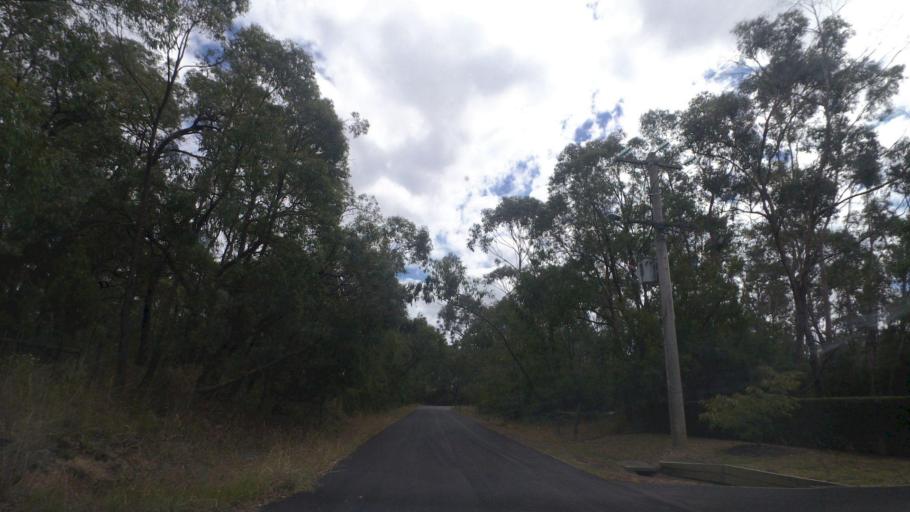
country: AU
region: Victoria
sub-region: Maroondah
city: Kilsyth South
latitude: -37.8288
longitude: 145.3102
